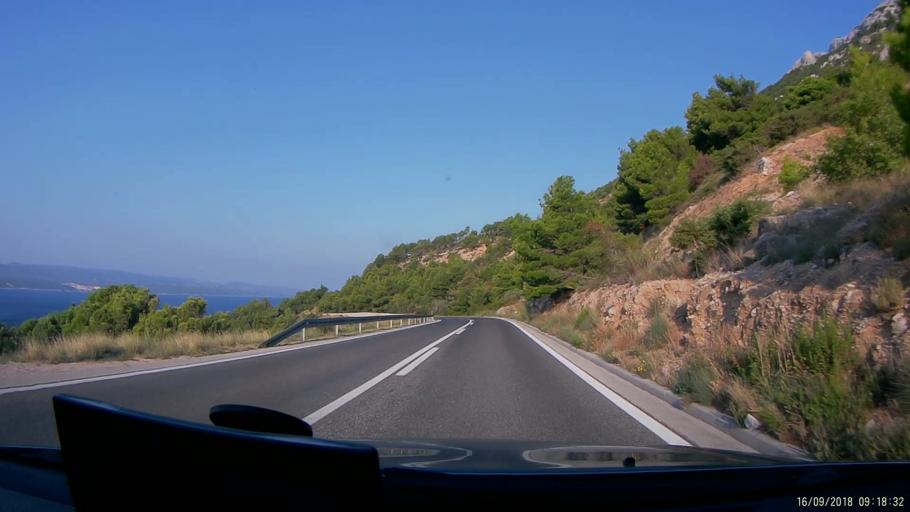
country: HR
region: Splitsko-Dalmatinska
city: Donja Brela
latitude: 43.4035
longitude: 16.8415
